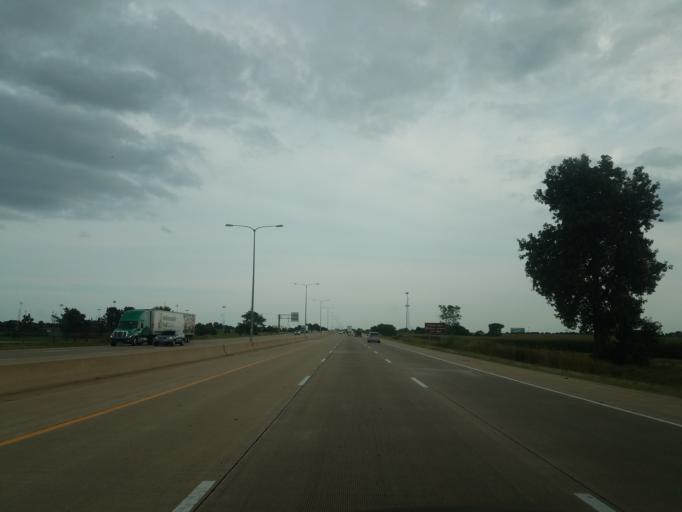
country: US
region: Illinois
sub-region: McLean County
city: Normal
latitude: 40.5234
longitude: -89.0281
